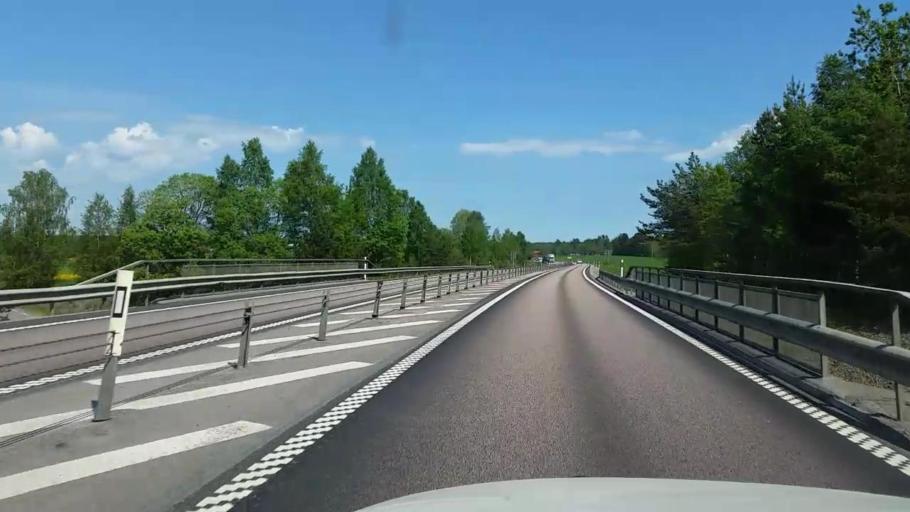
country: SE
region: Gaevleborg
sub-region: Hudiksvalls Kommun
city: Hudiksvall
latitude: 61.7544
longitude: 17.0845
